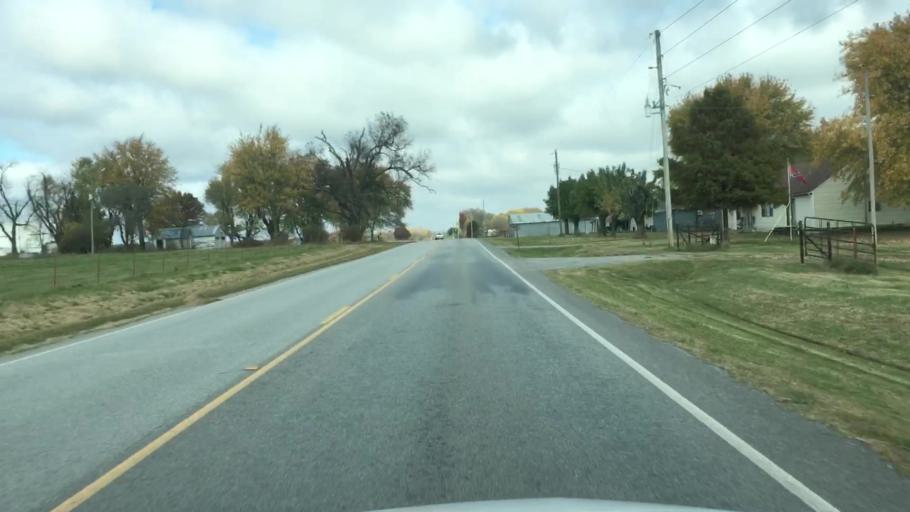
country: US
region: Arkansas
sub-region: Benton County
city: Centerton
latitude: 36.2729
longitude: -94.3502
